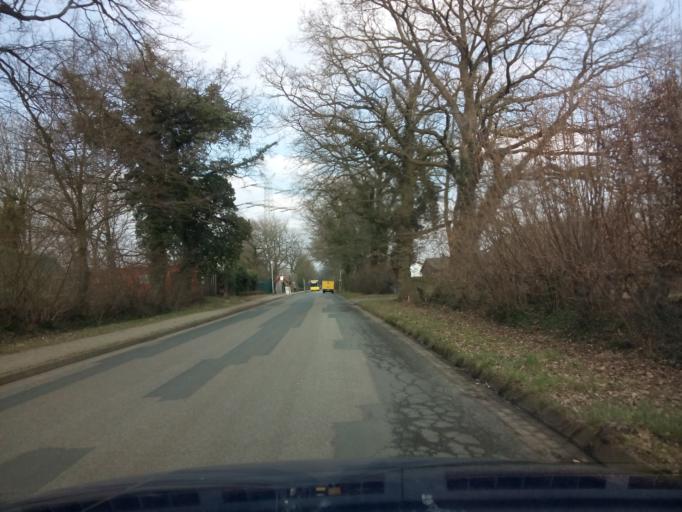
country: DE
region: Lower Saxony
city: Osterholz-Scharmbeck
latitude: 53.2264
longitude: 8.7635
